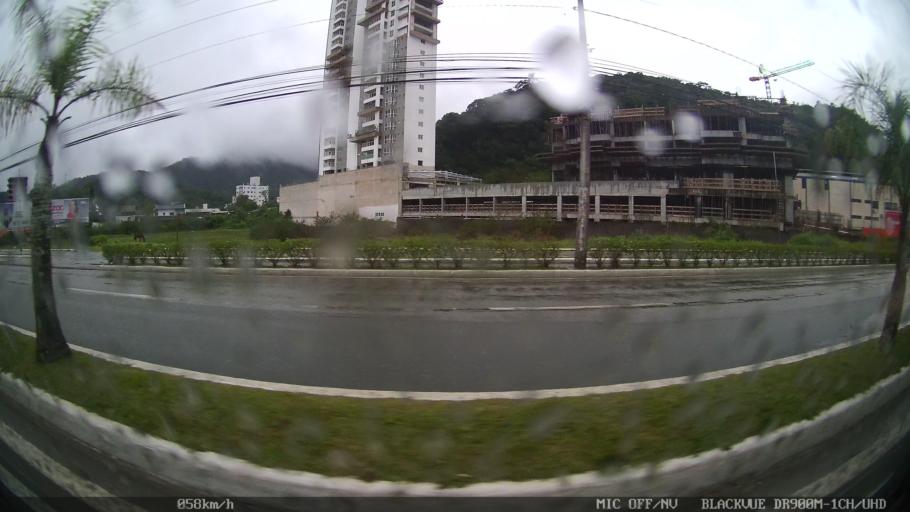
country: BR
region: Santa Catarina
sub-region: Itajai
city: Itajai
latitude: -26.9262
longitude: -48.6800
